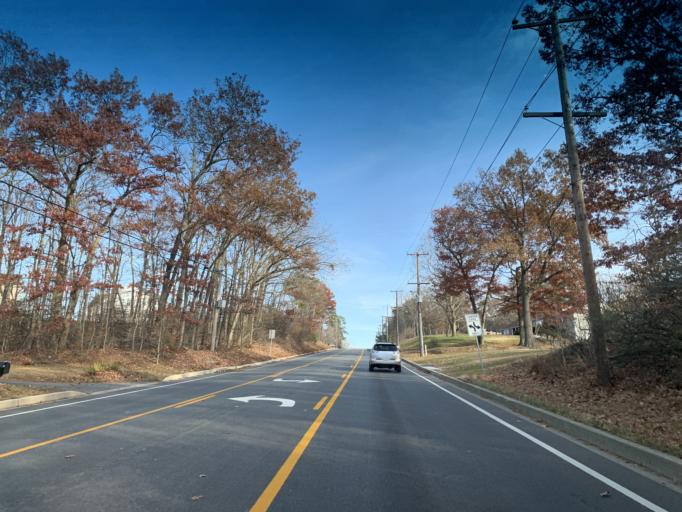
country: US
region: Maryland
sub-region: Cecil County
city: North East
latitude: 39.6026
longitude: -75.9212
